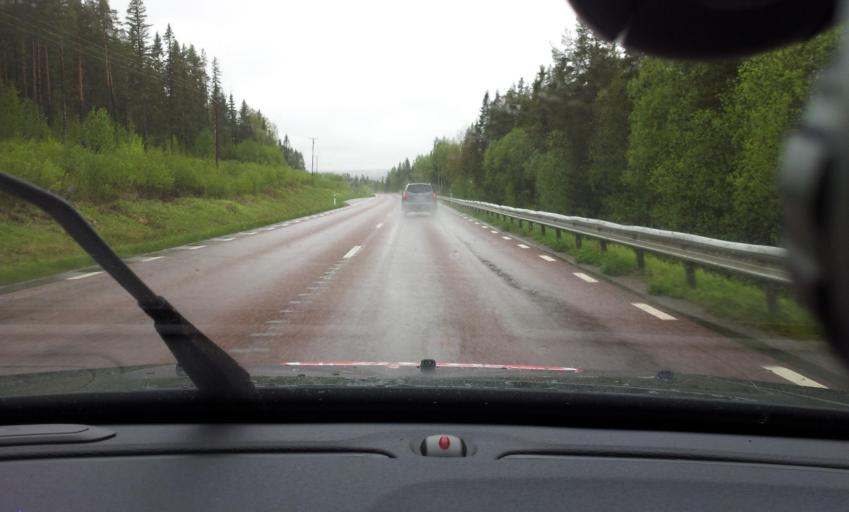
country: SE
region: Jaemtland
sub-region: Bergs Kommun
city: Hoverberg
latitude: 62.7796
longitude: 14.4517
